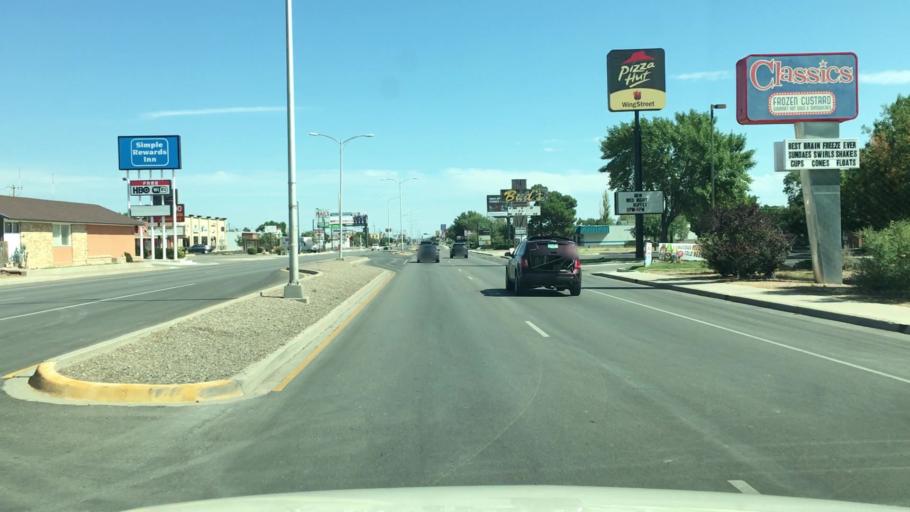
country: US
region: New Mexico
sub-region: Chaves County
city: Roswell
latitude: 33.4333
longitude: -104.5231
